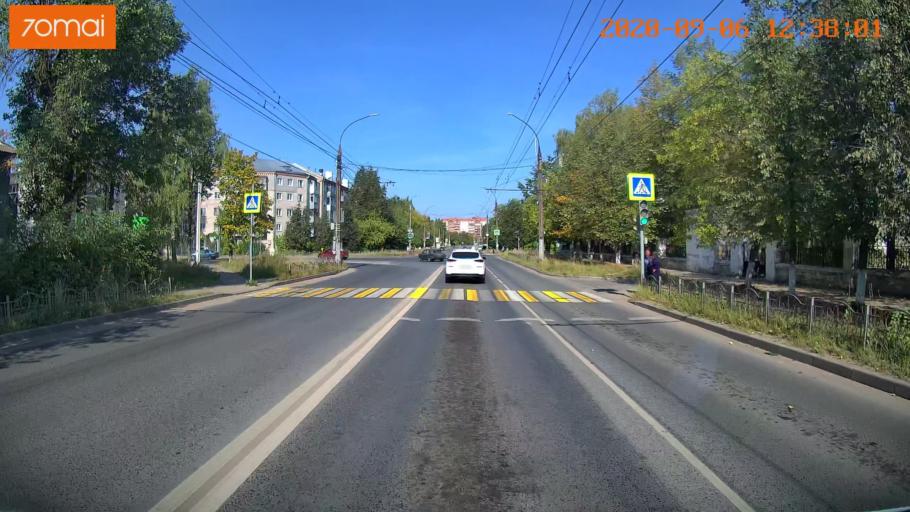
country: RU
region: Ivanovo
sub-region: Gorod Ivanovo
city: Ivanovo
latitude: 57.0300
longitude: 40.9805
